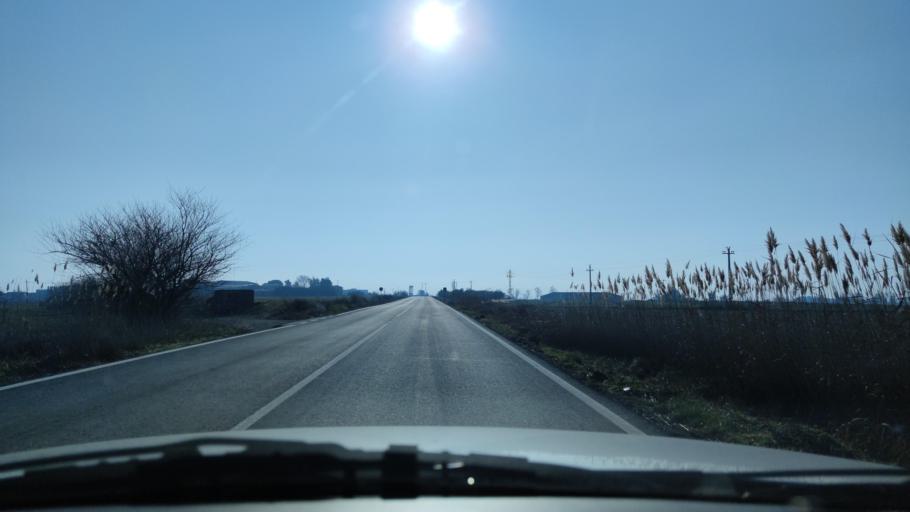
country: ES
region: Catalonia
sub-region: Provincia de Lleida
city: Torrefarrera
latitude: 41.7032
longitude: 0.6256
